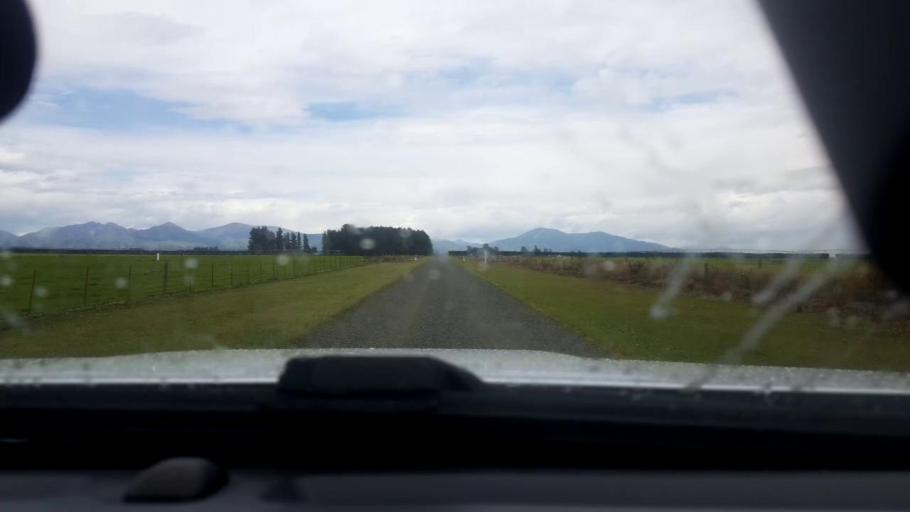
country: NZ
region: Canterbury
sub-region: Timaru District
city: Pleasant Point
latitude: -44.1134
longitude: 171.3540
